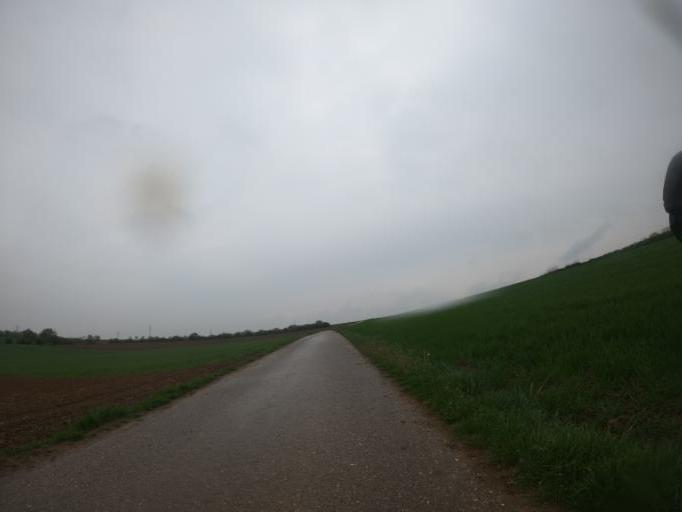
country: DE
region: Baden-Wuerttemberg
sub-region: Regierungsbezirk Stuttgart
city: Hemmingen
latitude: 48.8849
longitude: 9.0373
